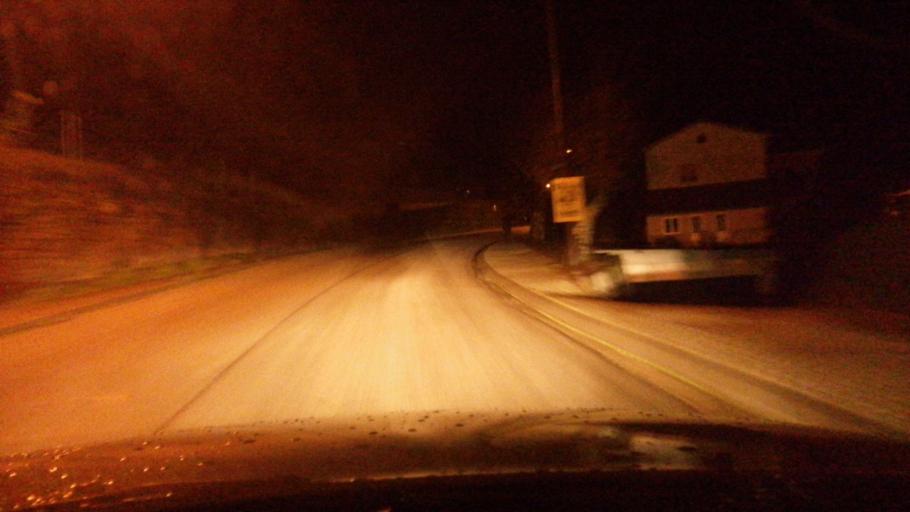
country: PT
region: Viseu
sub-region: Armamar
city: Armamar
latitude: 41.0607
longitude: -7.6452
